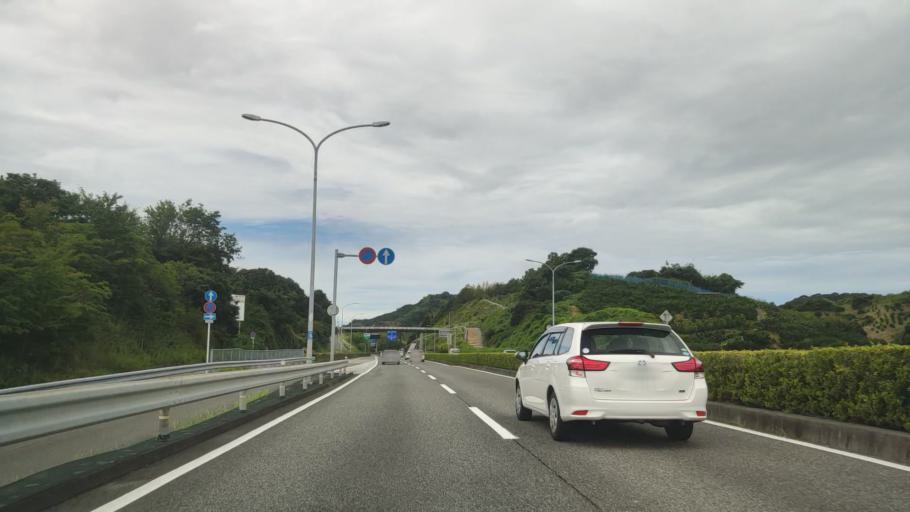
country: JP
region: Wakayama
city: Tanabe
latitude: 33.7441
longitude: 135.3843
